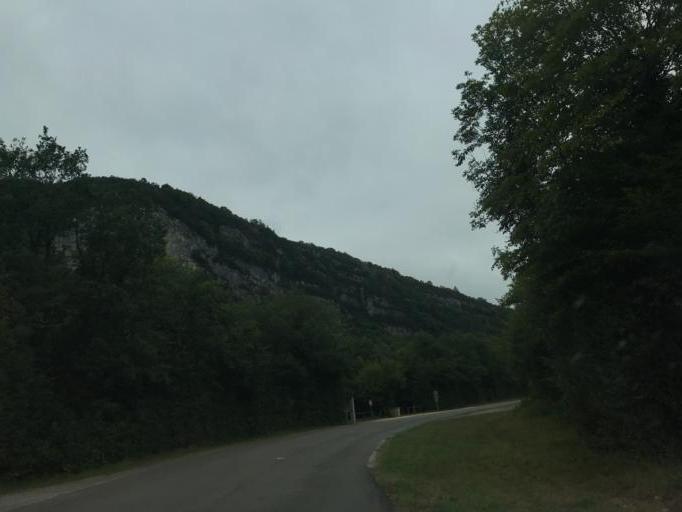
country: FR
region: Rhone-Alpes
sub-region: Departement de l'Ain
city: Dortan
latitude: 46.3444
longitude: 5.6332
